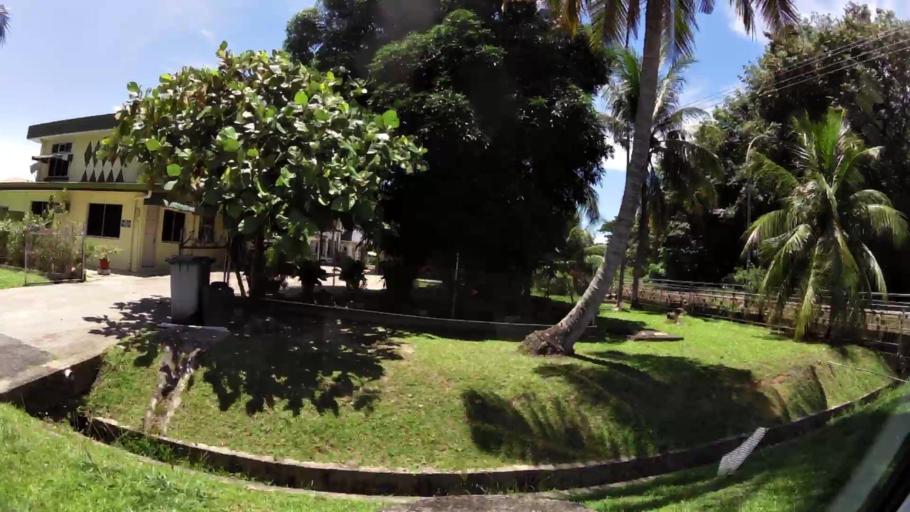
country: BN
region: Brunei and Muara
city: Bandar Seri Begawan
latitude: 4.9311
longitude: 114.9335
